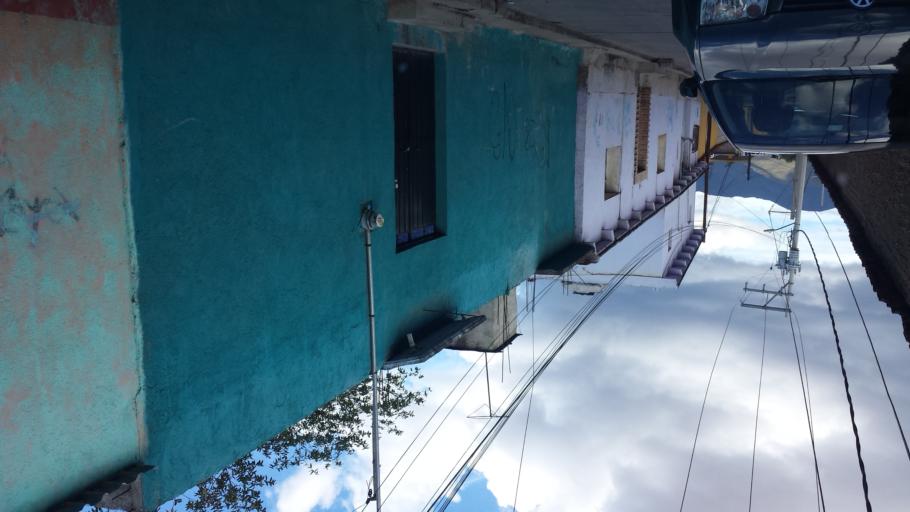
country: MX
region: Oaxaca
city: Tlacolula de Matamoros
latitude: 16.9581
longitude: -96.4787
